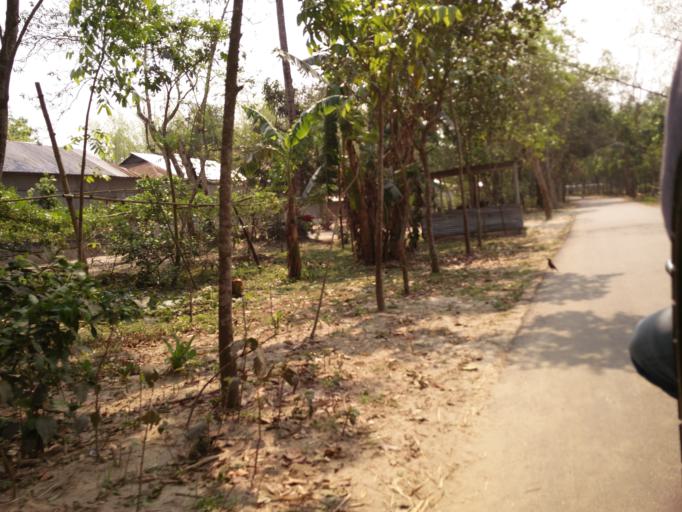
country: BD
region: Dhaka
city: Muktagacha
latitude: 24.8931
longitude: 90.2646
